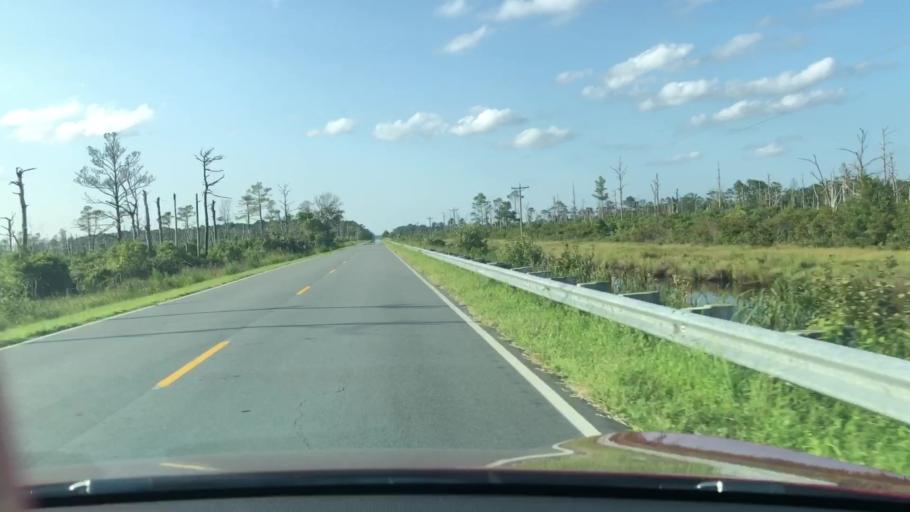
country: US
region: North Carolina
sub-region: Dare County
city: Wanchese
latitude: 35.6610
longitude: -75.7774
